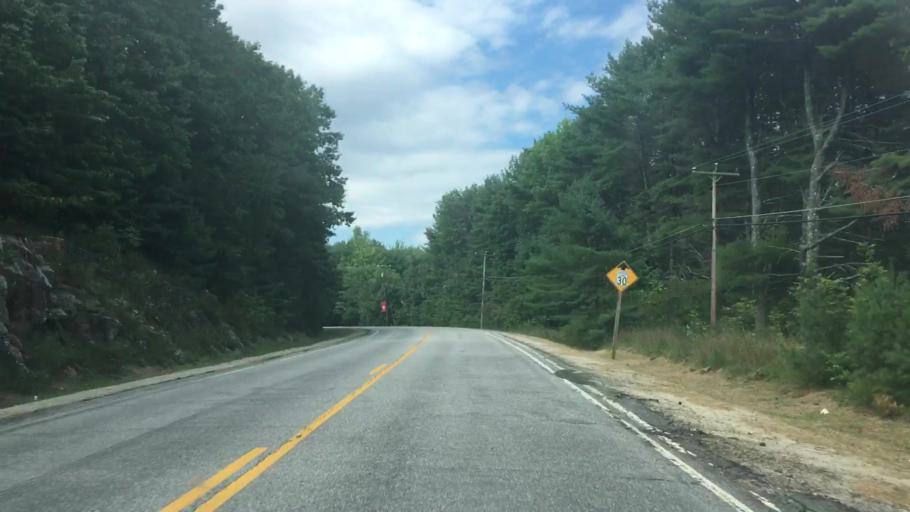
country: US
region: Maine
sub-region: Cumberland County
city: Raymond
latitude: 43.9993
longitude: -70.5192
